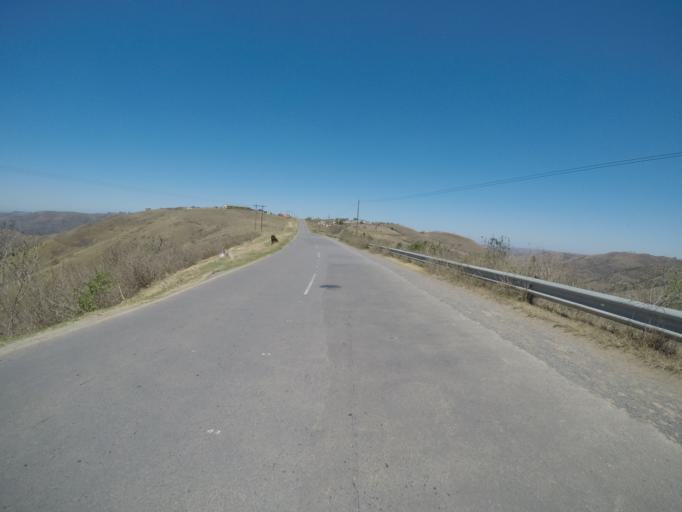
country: ZA
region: Eastern Cape
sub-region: OR Tambo District Municipality
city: Mthatha
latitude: -31.9023
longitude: 28.9463
